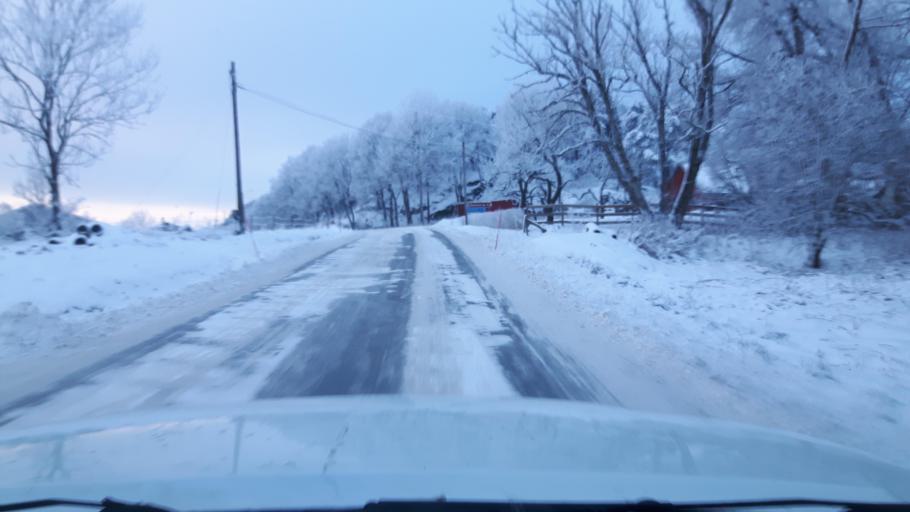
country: SE
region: Halland
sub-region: Kungsbacka Kommun
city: Frillesas
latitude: 57.3316
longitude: 12.2440
